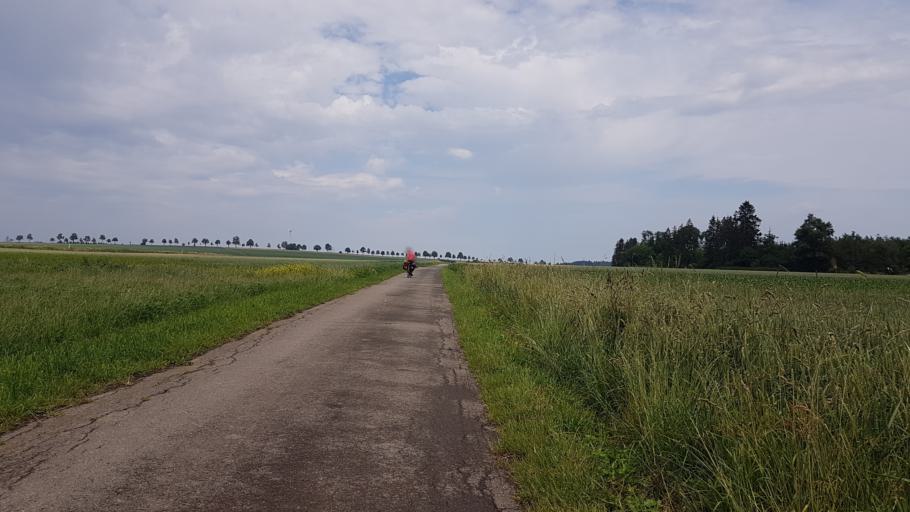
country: DE
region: Baden-Wuerttemberg
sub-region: Freiburg Region
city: Hufingen
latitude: 47.8823
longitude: 8.4747
